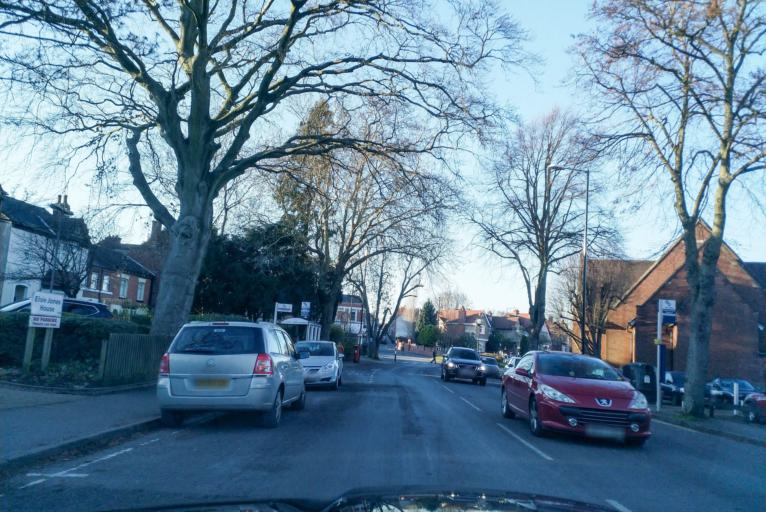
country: GB
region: England
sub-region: Coventry
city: Coventry
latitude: 52.3993
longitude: -1.5296
